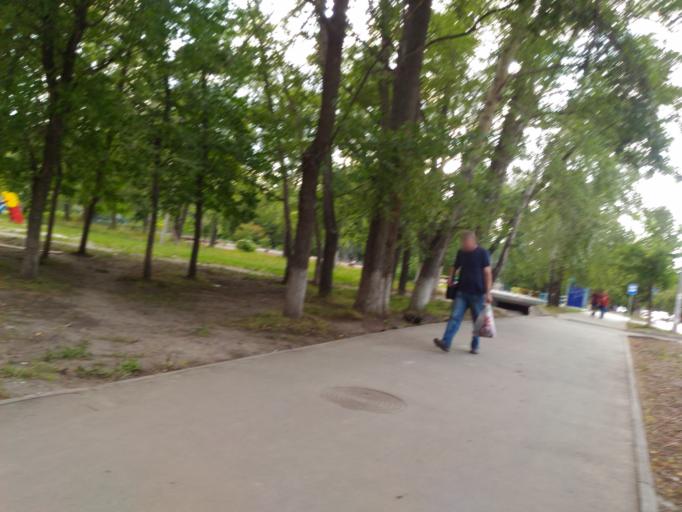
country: RU
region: Ulyanovsk
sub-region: Ulyanovskiy Rayon
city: Ulyanovsk
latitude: 54.2829
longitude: 48.2900
